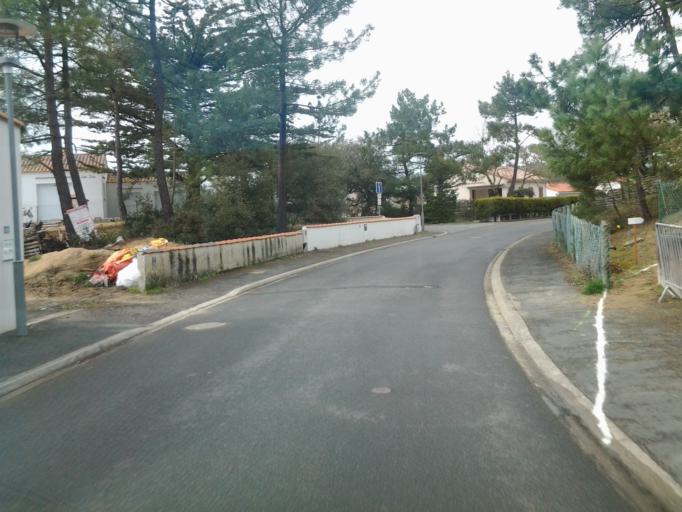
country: FR
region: Pays de la Loire
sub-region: Departement de la Vendee
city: La Tranche-sur-Mer
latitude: 46.3448
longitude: -1.4624
